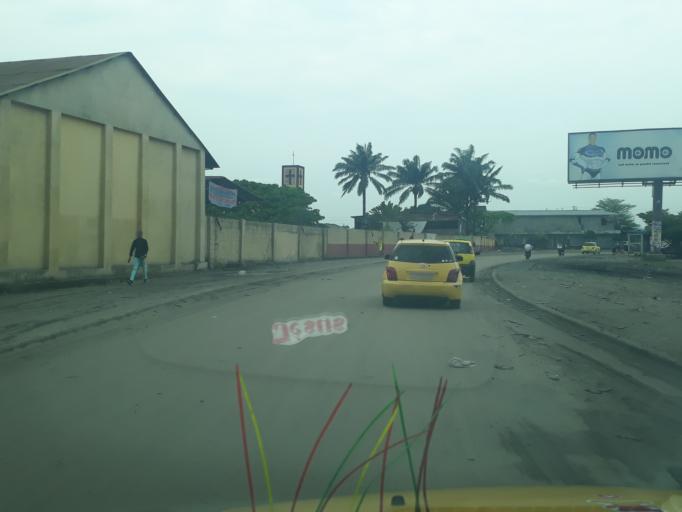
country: CD
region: Kinshasa
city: Kinshasa
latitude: -4.3426
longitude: 15.3040
